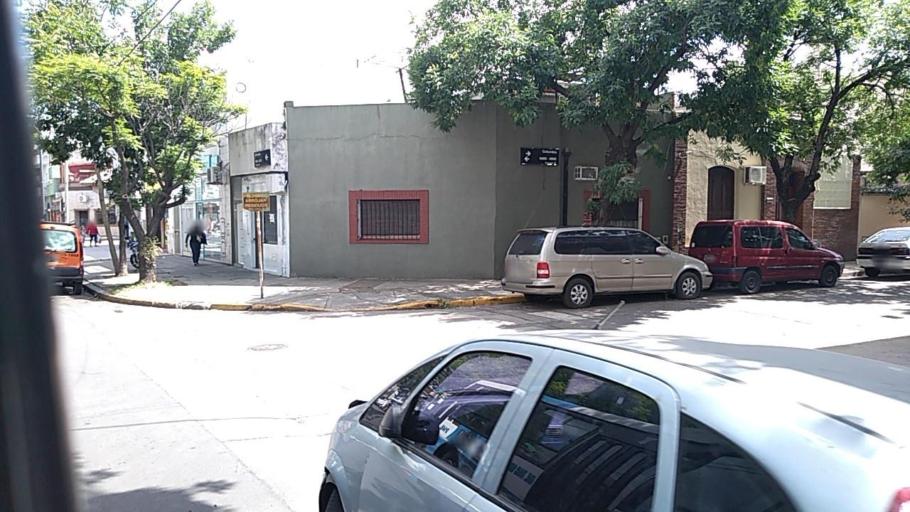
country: AR
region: Buenos Aires F.D.
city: Villa Santa Rita
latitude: -34.6171
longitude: -58.5125
